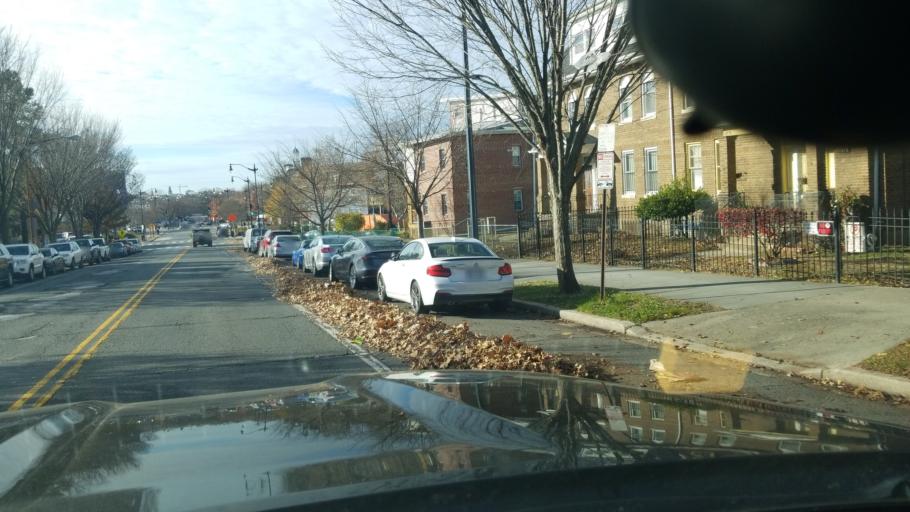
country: US
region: Maryland
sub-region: Montgomery County
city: Takoma Park
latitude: 38.9440
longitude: -77.0244
